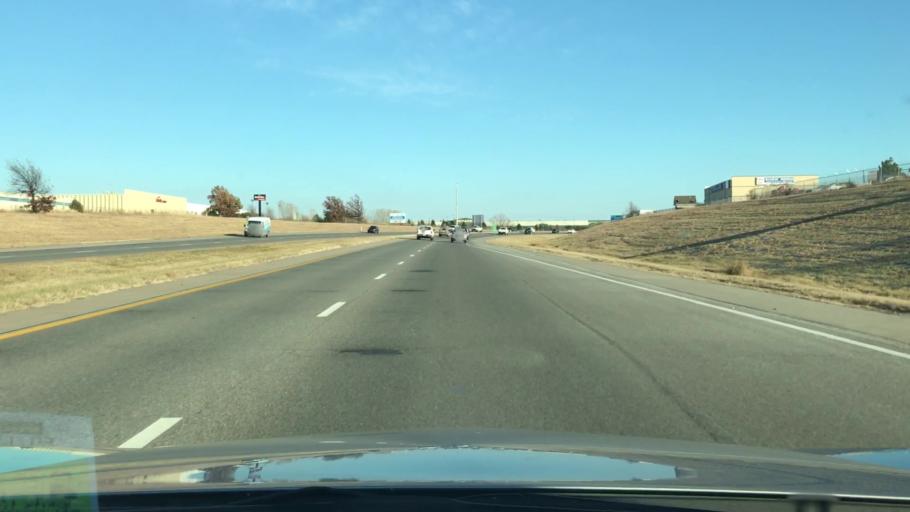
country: US
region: Kansas
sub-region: Sedgwick County
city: Bellaire
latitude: 37.7443
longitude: -97.2386
